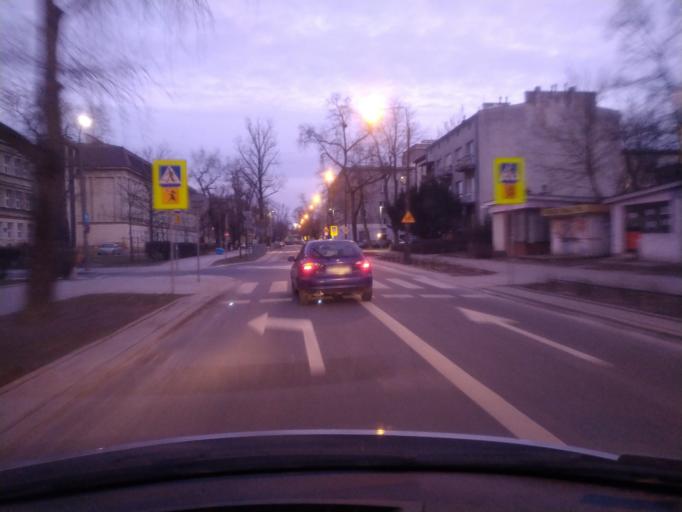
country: PL
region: Masovian Voivodeship
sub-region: Warszawa
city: Praga Poludnie
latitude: 52.2411
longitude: 21.0780
